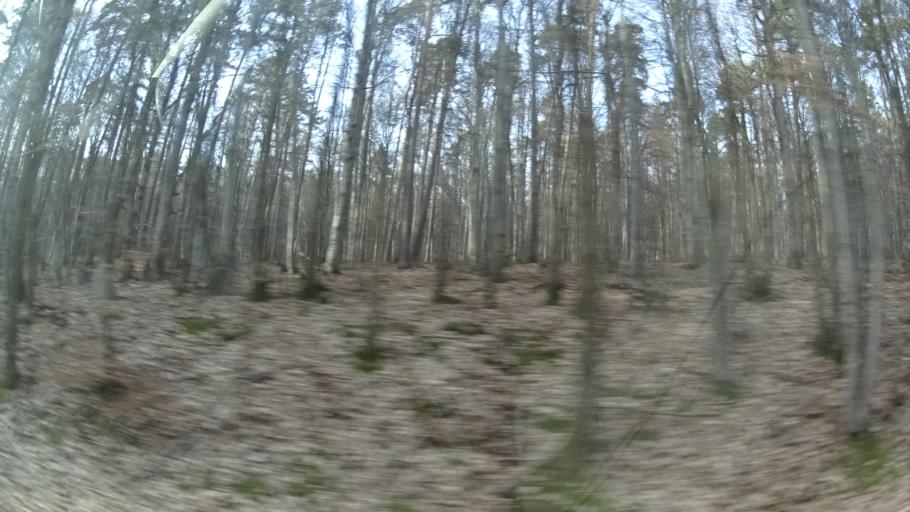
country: DE
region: Bavaria
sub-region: Regierungsbezirk Unterfranken
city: Sandberg
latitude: 50.3258
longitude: 9.9957
